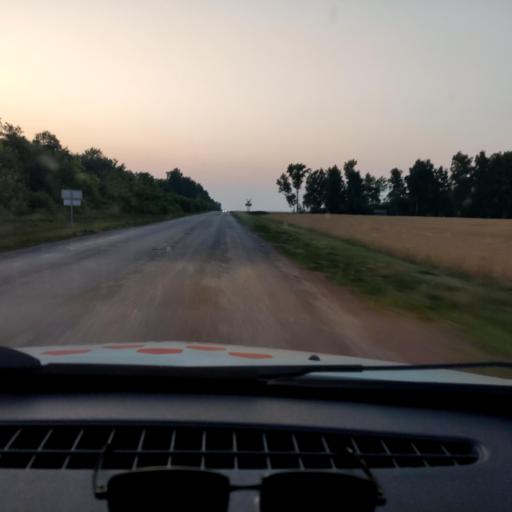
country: RU
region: Bashkortostan
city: Ulukulevo
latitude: 54.3861
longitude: 56.3824
